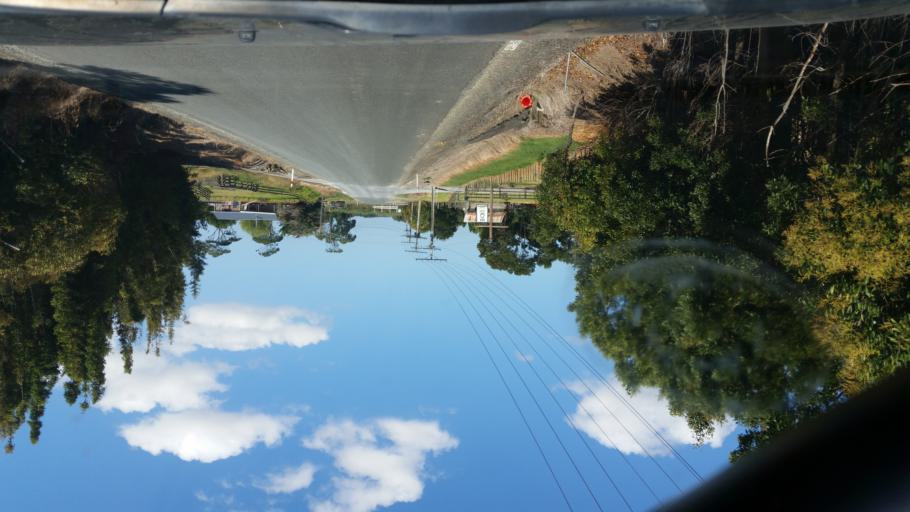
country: NZ
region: Northland
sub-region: Kaipara District
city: Dargaville
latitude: -35.9442
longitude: 173.8542
